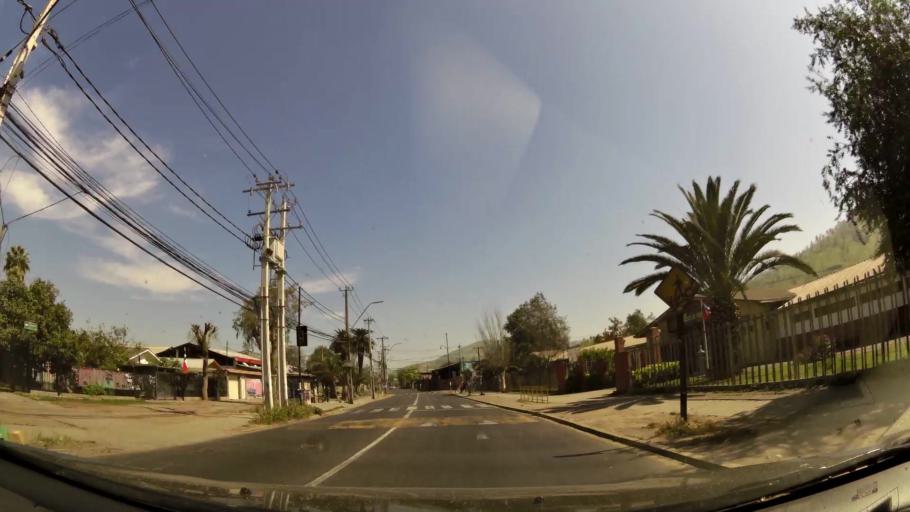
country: CL
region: Santiago Metropolitan
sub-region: Provincia de Santiago
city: Lo Prado
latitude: -33.4026
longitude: -70.7115
